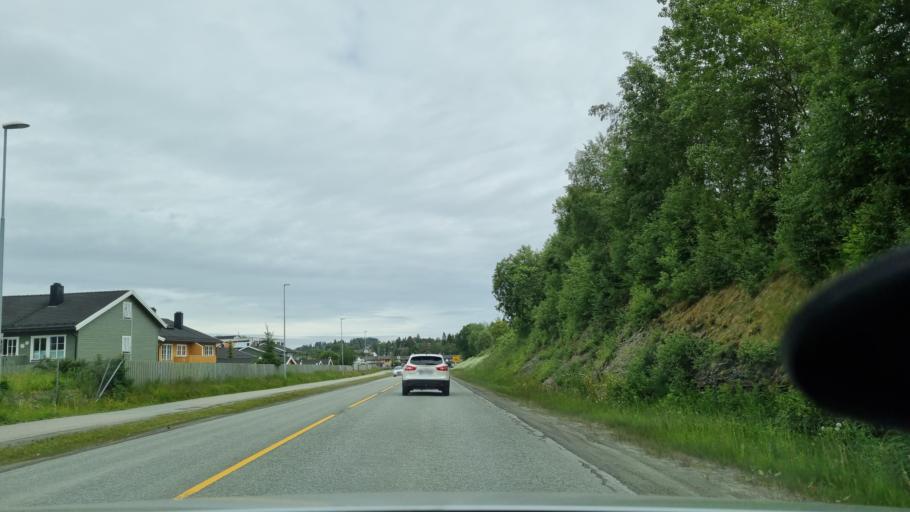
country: NO
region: Sor-Trondelag
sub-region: Trondheim
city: Trondheim
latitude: 63.3852
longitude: 10.3246
